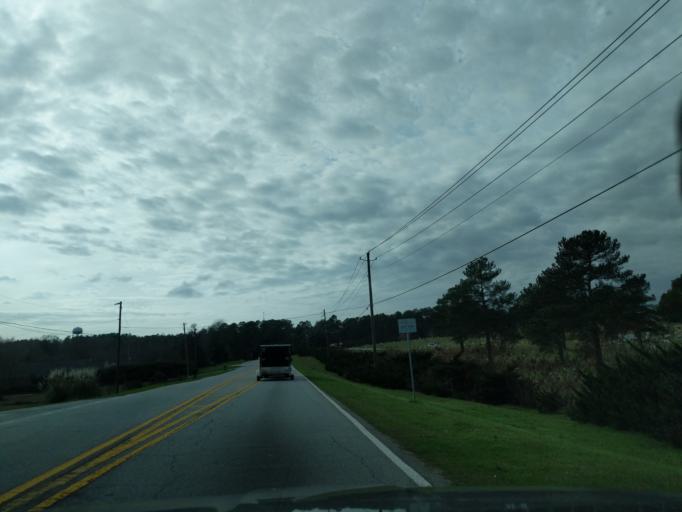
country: US
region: Georgia
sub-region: Columbia County
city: Grovetown
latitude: 33.4746
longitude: -82.1450
